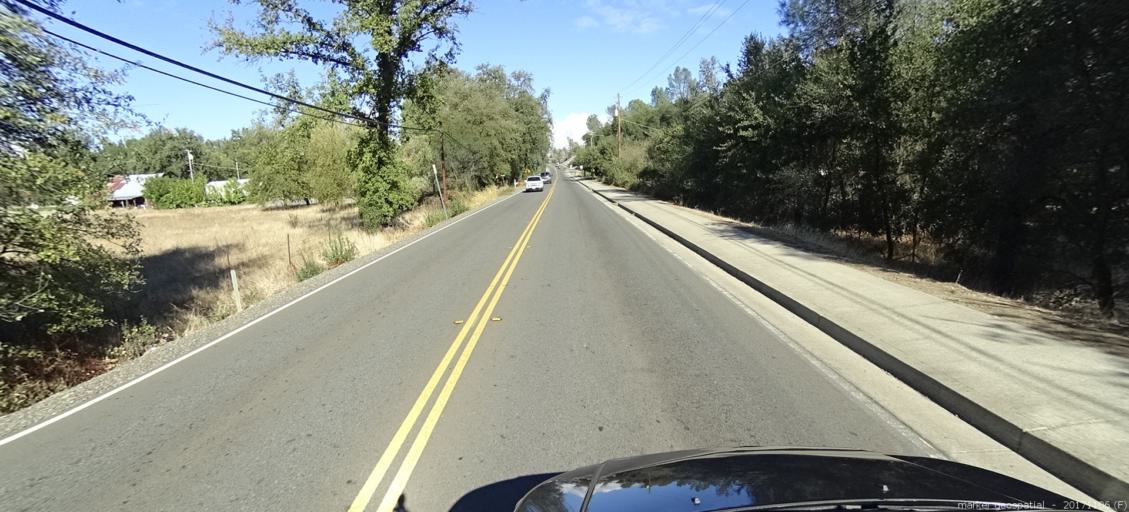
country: US
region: California
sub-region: Shasta County
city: Palo Cedro
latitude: 40.5657
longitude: -122.2386
